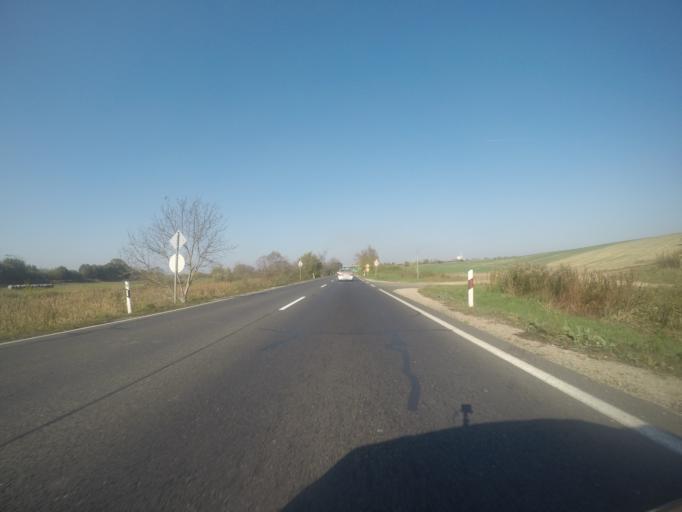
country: HU
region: Fejer
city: Baracs
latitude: 46.9047
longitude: 18.9247
